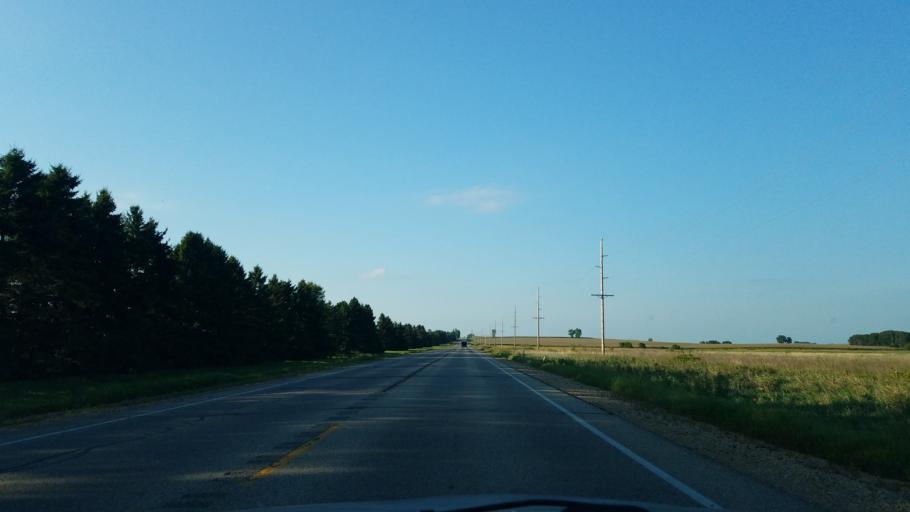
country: US
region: Wisconsin
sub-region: Saint Croix County
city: Roberts
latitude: 45.0090
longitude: -92.5378
